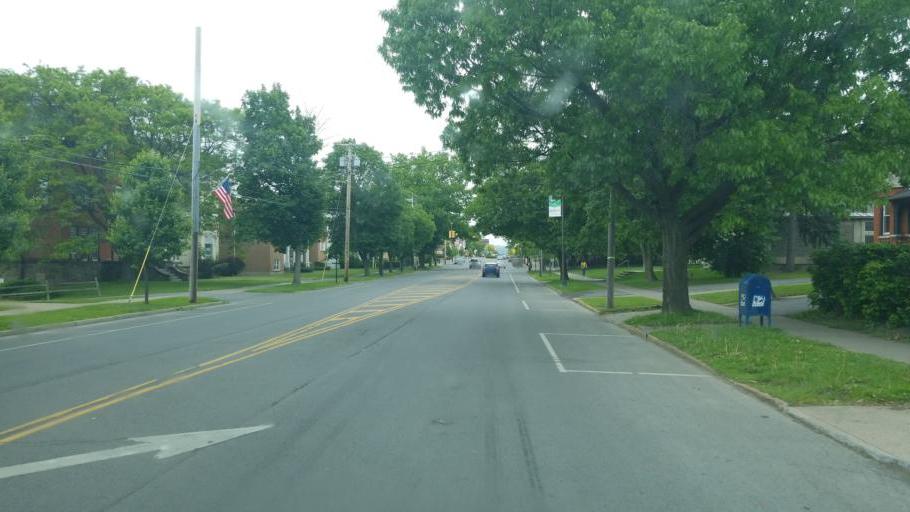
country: US
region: New York
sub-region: Oneida County
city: Utica
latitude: 43.0947
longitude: -75.2450
